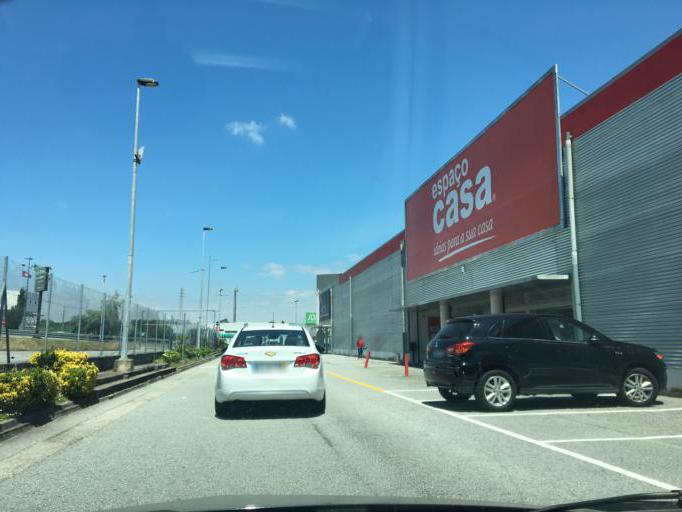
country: PT
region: Porto
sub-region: Maia
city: Maia
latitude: 41.2476
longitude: -8.6214
